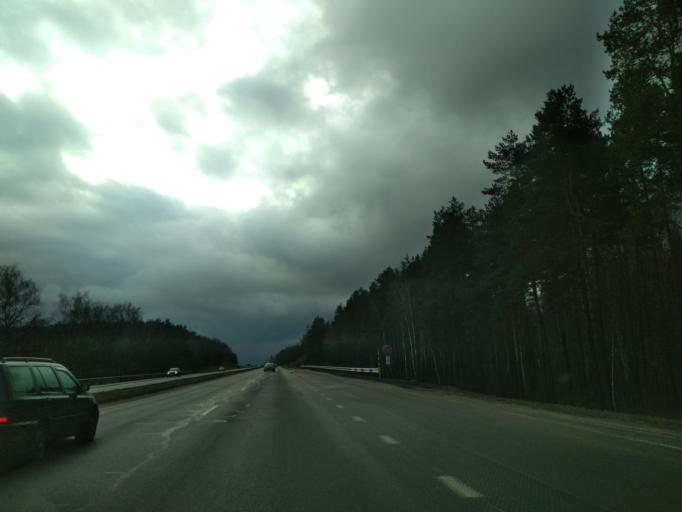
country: BY
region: Minsk
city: Luhavaya Slabada
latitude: 53.7718
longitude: 27.8270
